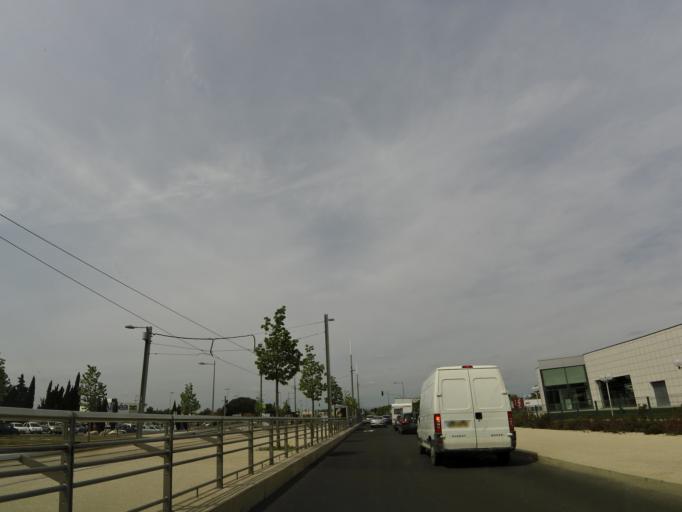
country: FR
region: Languedoc-Roussillon
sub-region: Departement de l'Herault
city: Perols
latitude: 43.5726
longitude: 3.9465
